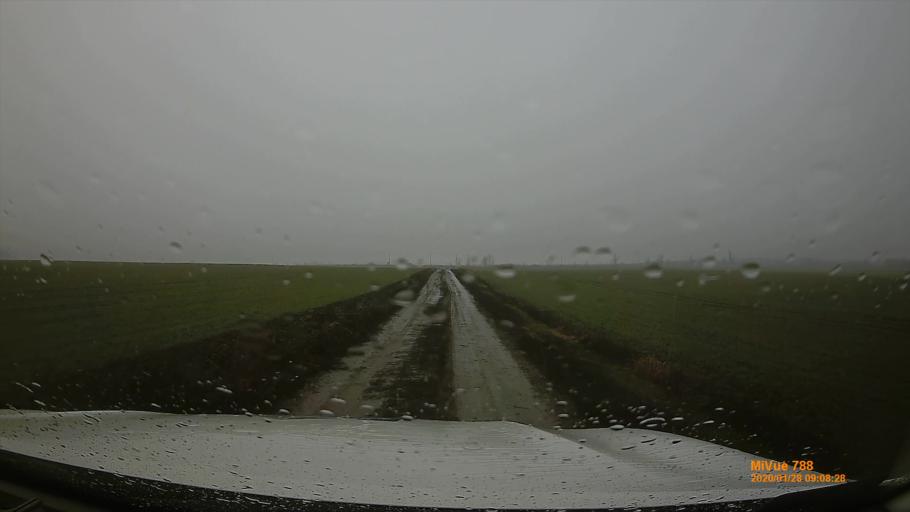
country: HU
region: Pest
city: Pilis
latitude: 47.3126
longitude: 19.5448
